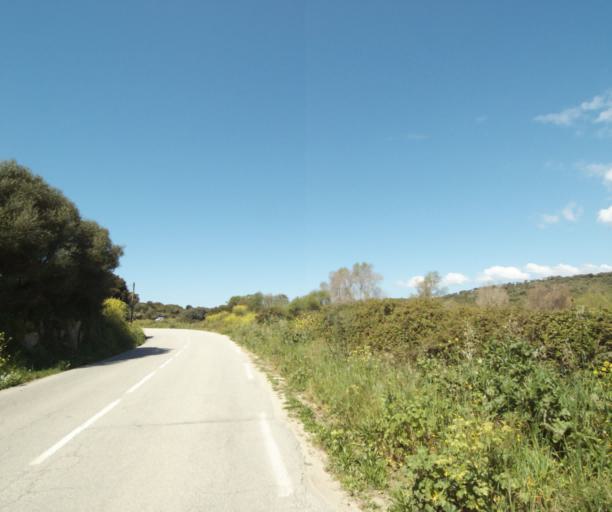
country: FR
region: Corsica
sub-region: Departement de la Corse-du-Sud
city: Propriano
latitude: 41.6576
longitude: 8.9022
